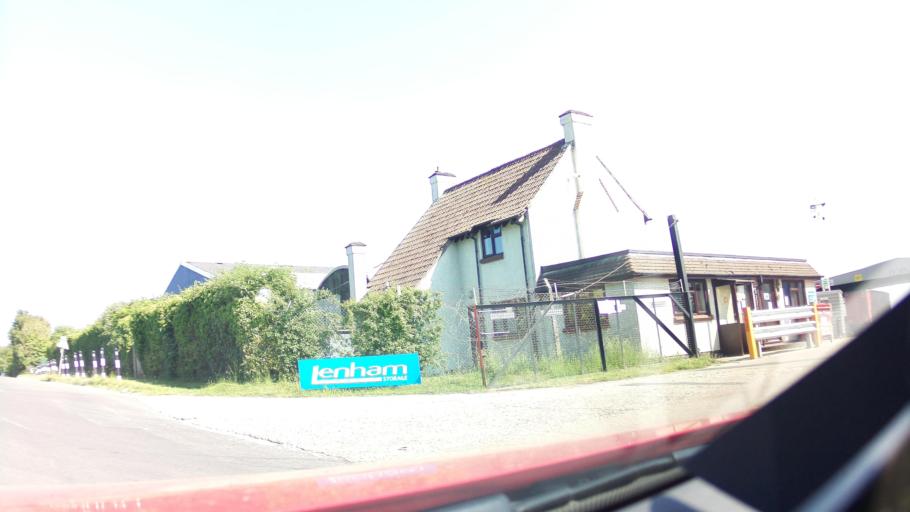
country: GB
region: England
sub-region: Hampshire
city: Abbotts Ann
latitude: 51.2193
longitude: -1.5670
